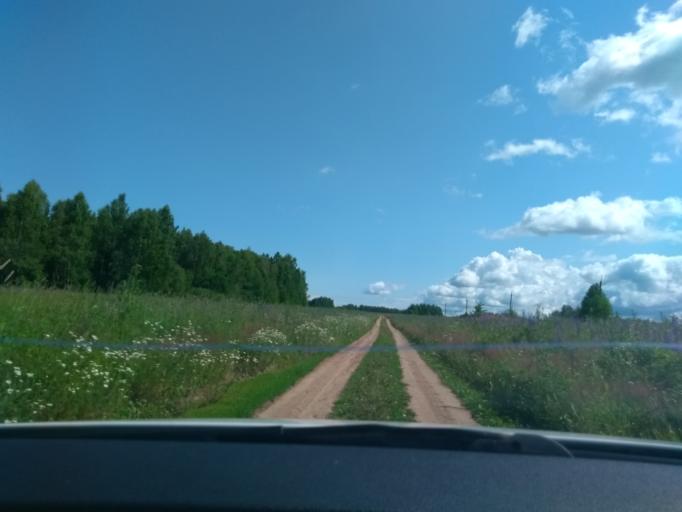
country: RU
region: Perm
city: Sylva
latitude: 57.8191
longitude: 56.7360
